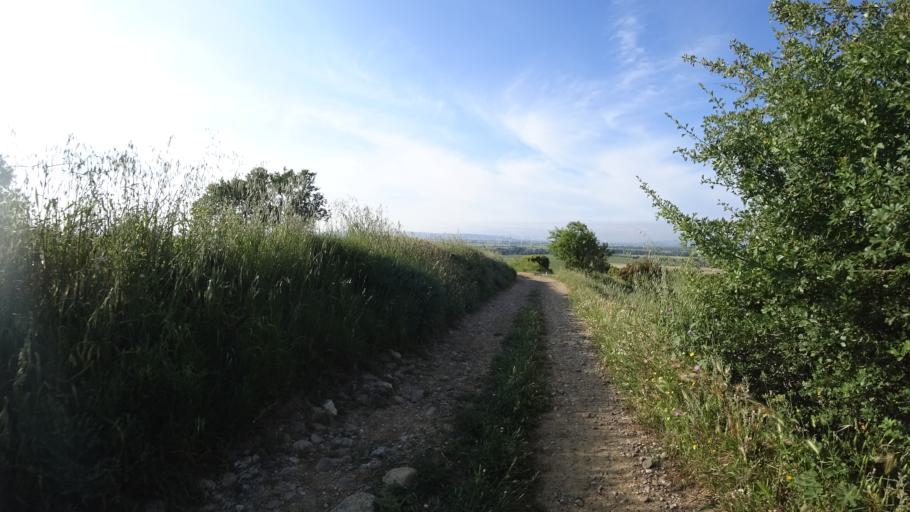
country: FR
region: Languedoc-Roussillon
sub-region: Departement de l'Aude
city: Canet
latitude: 43.2542
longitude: 2.8162
